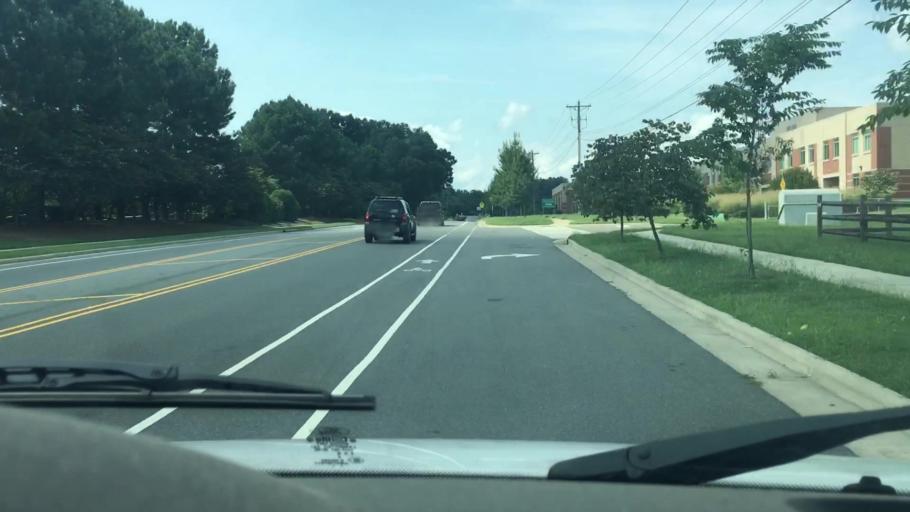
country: US
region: North Carolina
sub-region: Mecklenburg County
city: Huntersville
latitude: 35.4249
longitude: -80.8717
